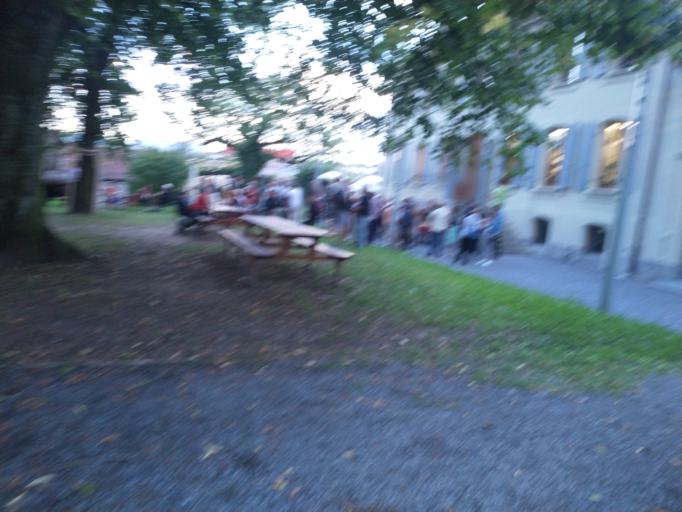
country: CH
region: Vaud
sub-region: Ouest Lausannois District
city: Prilly
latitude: 46.5338
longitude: 6.5903
